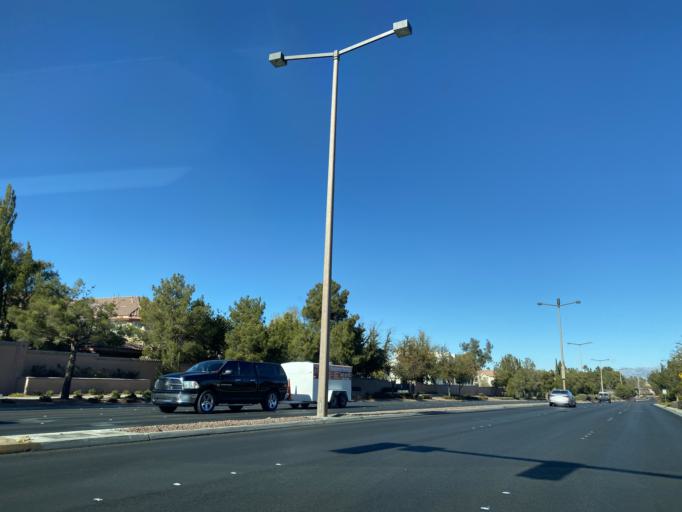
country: US
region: Nevada
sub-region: Clark County
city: Summerlin South
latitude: 36.1889
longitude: -115.2875
